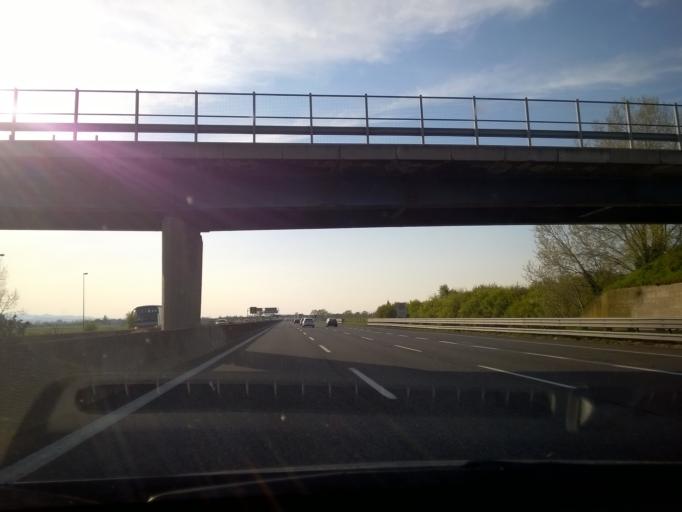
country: IT
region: Emilia-Romagna
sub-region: Provincia di Ravenna
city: Castel Bolognese
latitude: 44.3560
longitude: 11.8090
